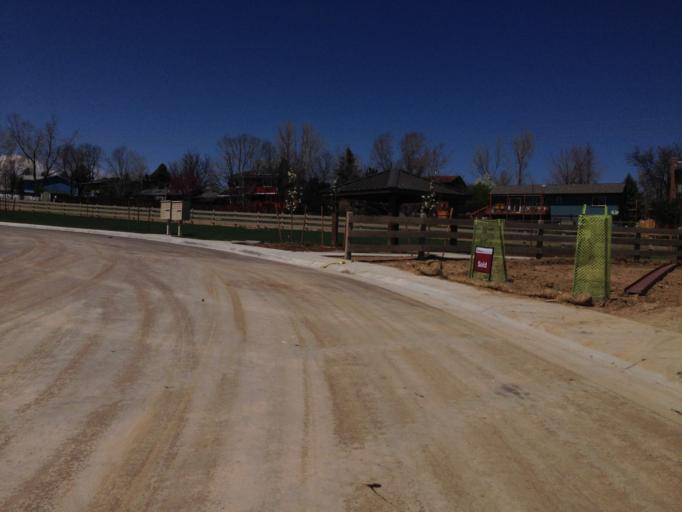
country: US
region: Colorado
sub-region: Boulder County
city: Louisville
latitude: 39.9901
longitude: -105.1166
